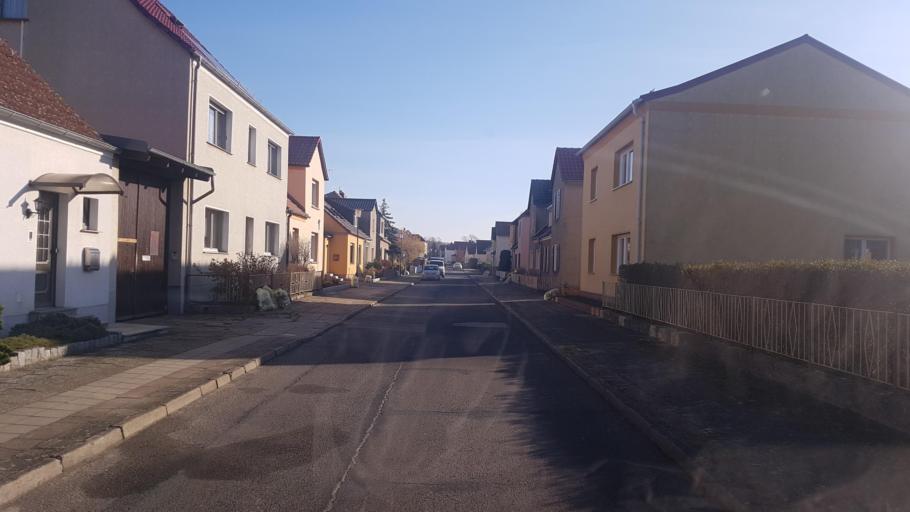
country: DE
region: Brandenburg
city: Niemegk
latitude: 52.0704
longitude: 12.6968
